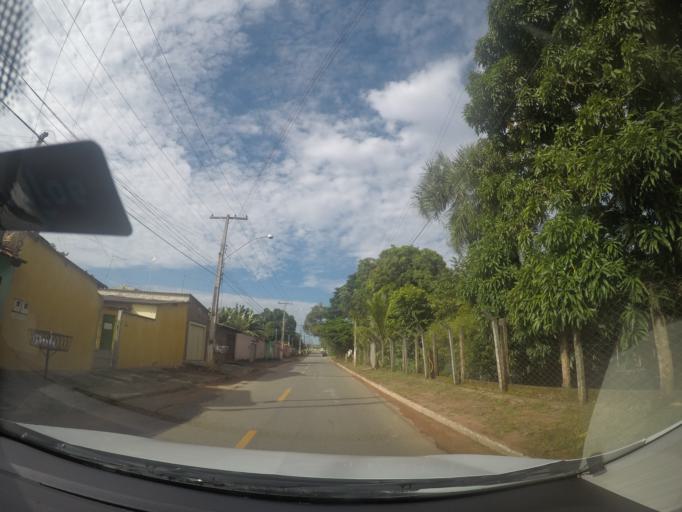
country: BR
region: Goias
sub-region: Goiania
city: Goiania
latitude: -16.6869
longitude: -49.1886
